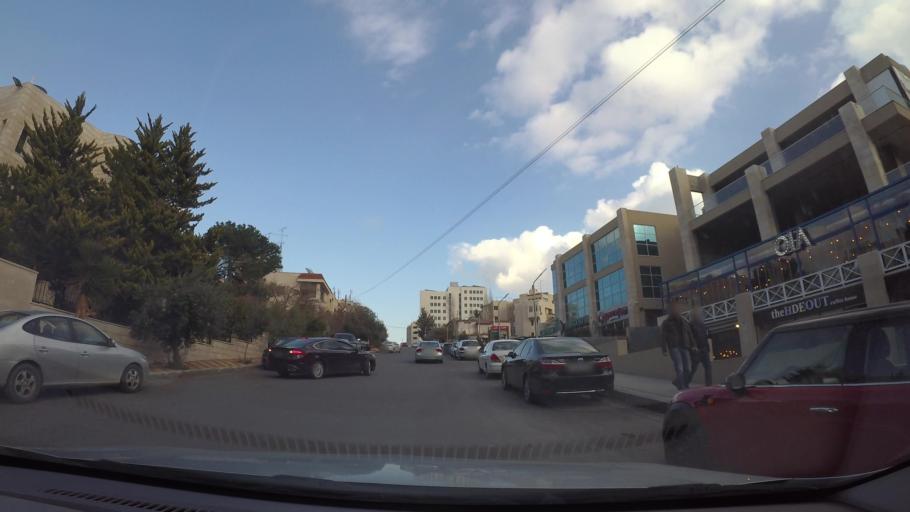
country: JO
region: Amman
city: Al Jubayhah
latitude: 31.9772
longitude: 35.8632
